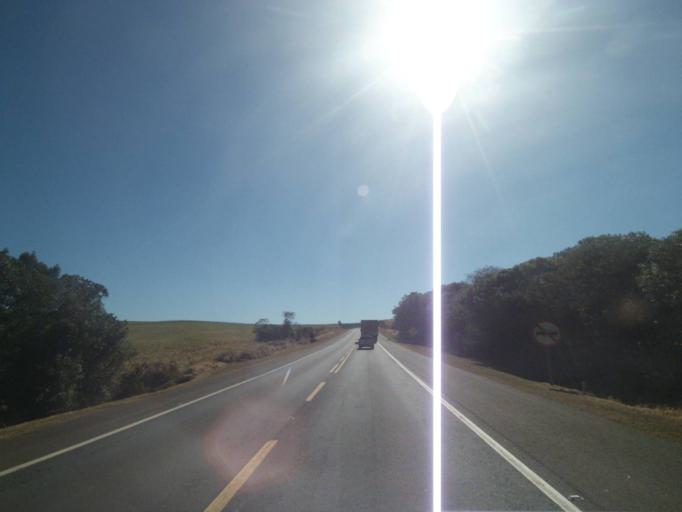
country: BR
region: Parana
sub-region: Tibagi
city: Tibagi
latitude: -24.7204
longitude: -50.5394
